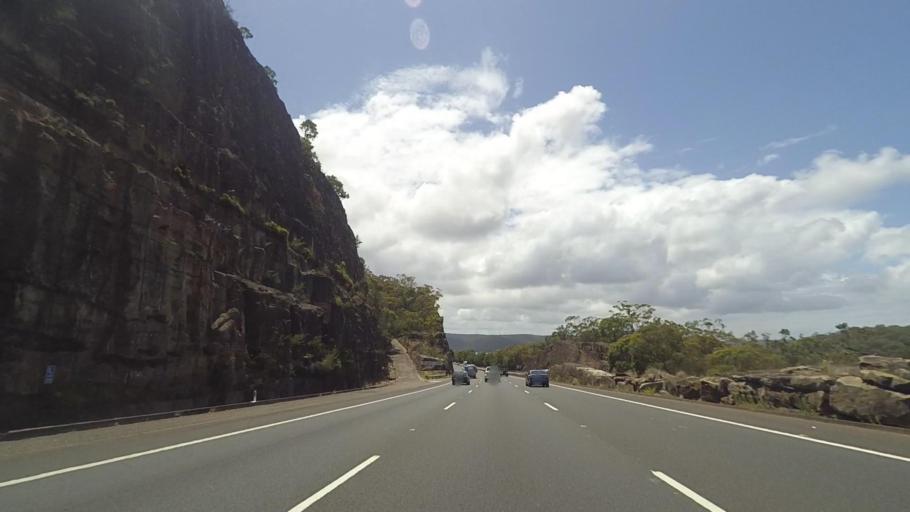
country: AU
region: New South Wales
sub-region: Hornsby Shire
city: Berowra
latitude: -33.5475
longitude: 151.1959
